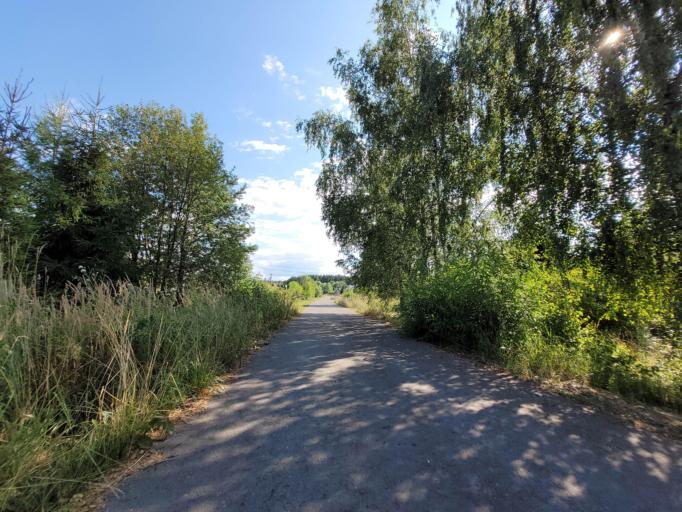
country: RU
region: Moskovskaya
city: Lopatinskiy
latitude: 55.3893
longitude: 38.7137
